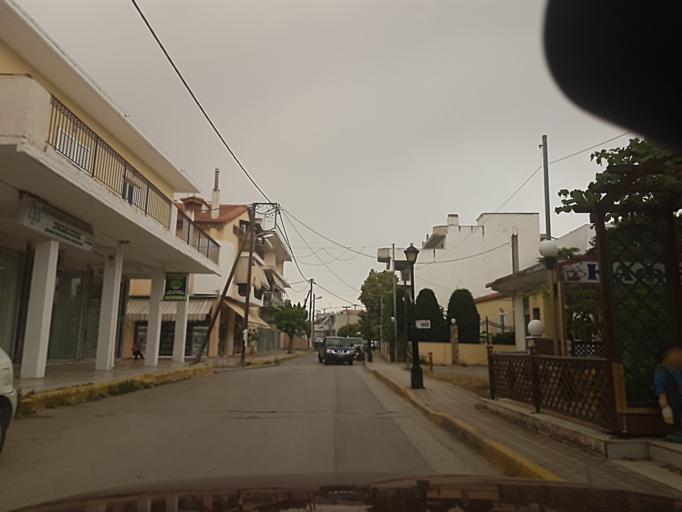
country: GR
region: Central Greece
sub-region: Nomos Evvoias
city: Vasilikon
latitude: 38.4269
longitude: 23.6696
